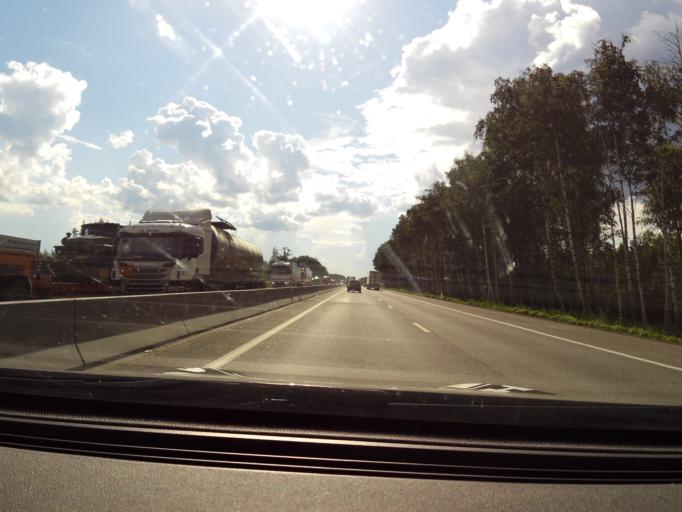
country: RU
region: Nizjnij Novgorod
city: Babino
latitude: 56.3034
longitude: 43.5987
